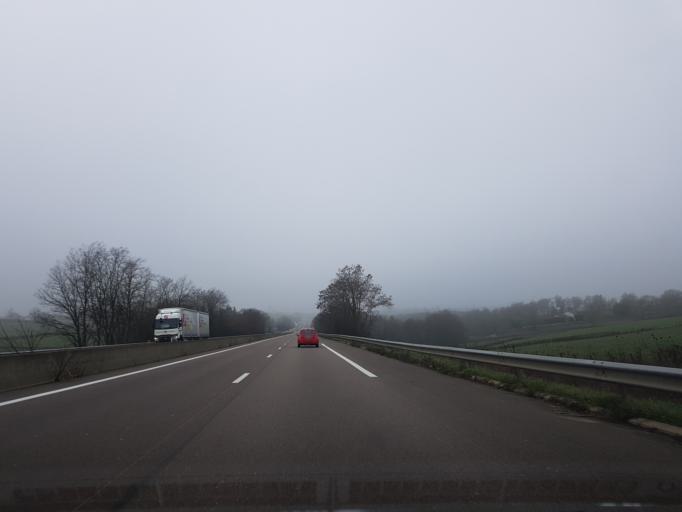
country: FR
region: Bourgogne
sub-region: Departement de Saone-et-Loire
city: Ecuisses
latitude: 46.7458
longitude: 4.5227
